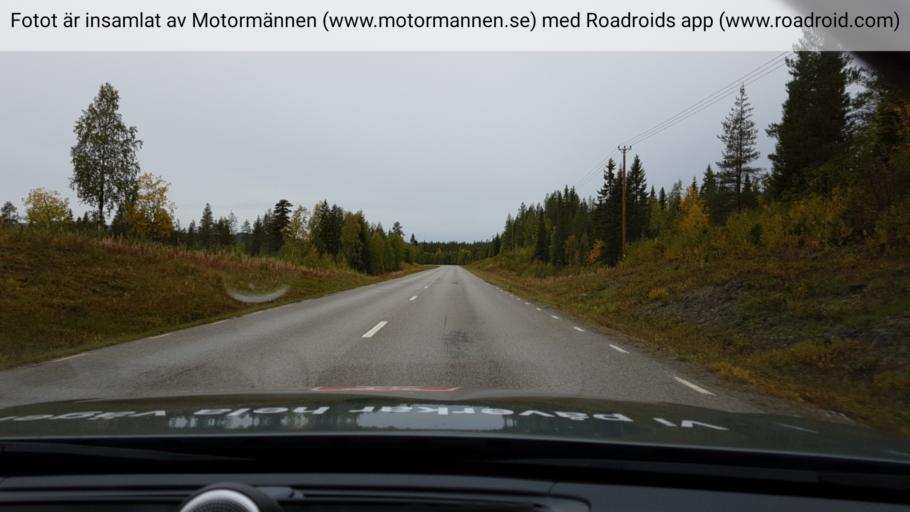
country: SE
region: Jaemtland
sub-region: Stroemsunds Kommun
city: Stroemsund
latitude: 64.3056
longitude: 15.2905
